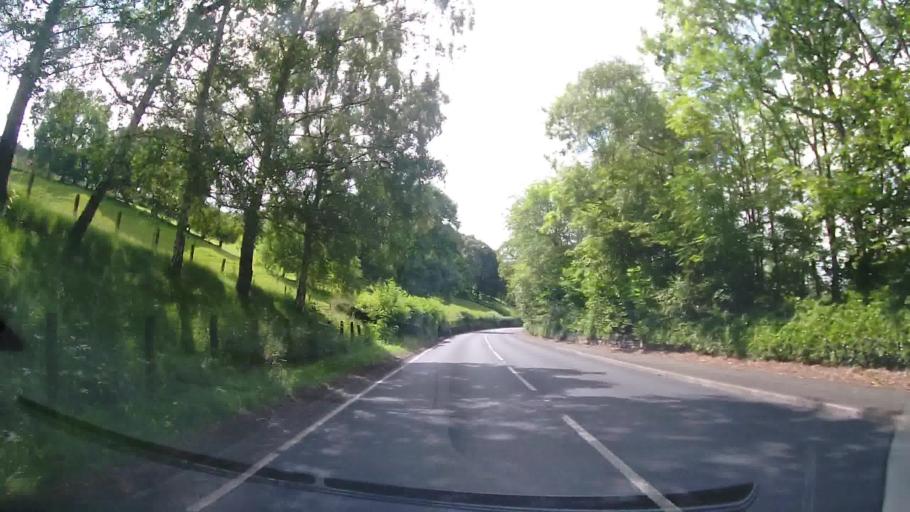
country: GB
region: Wales
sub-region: Denbighshire
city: Corwen
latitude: 52.9776
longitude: -3.3257
